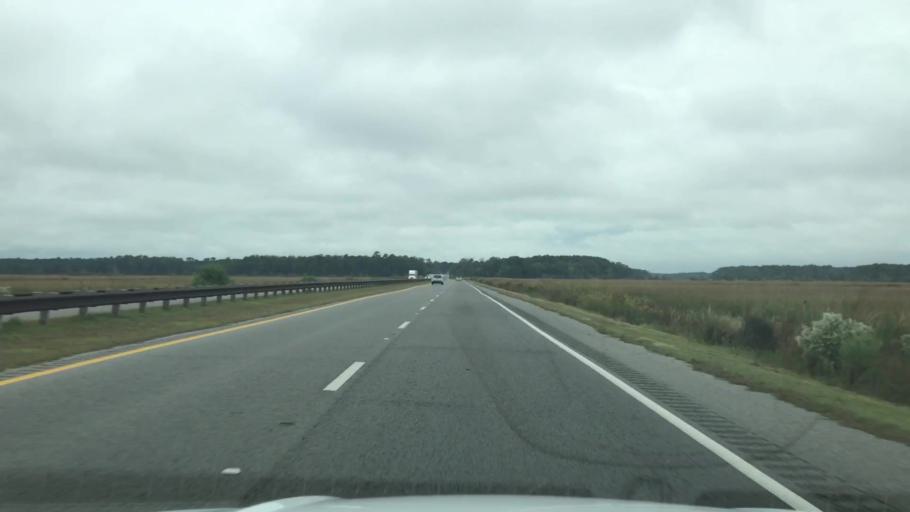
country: US
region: South Carolina
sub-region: Hampton County
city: Yemassee
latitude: 32.6565
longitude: -80.6725
